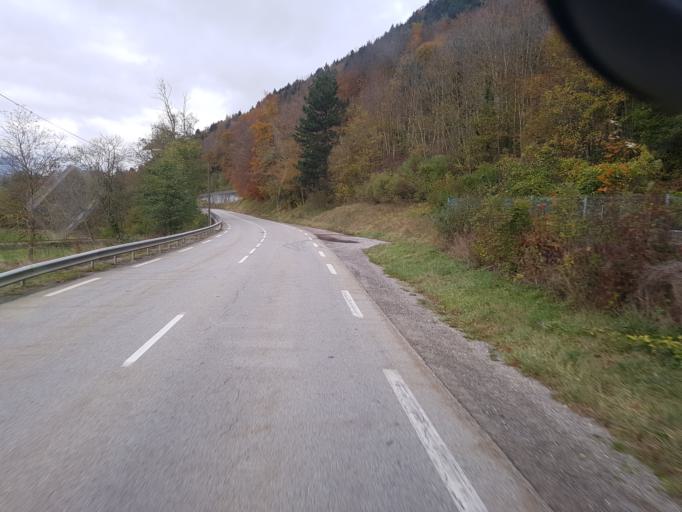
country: FR
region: Rhone-Alpes
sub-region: Departement de l'Isere
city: La Motte-Saint-Martin
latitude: 44.9332
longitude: 5.6406
